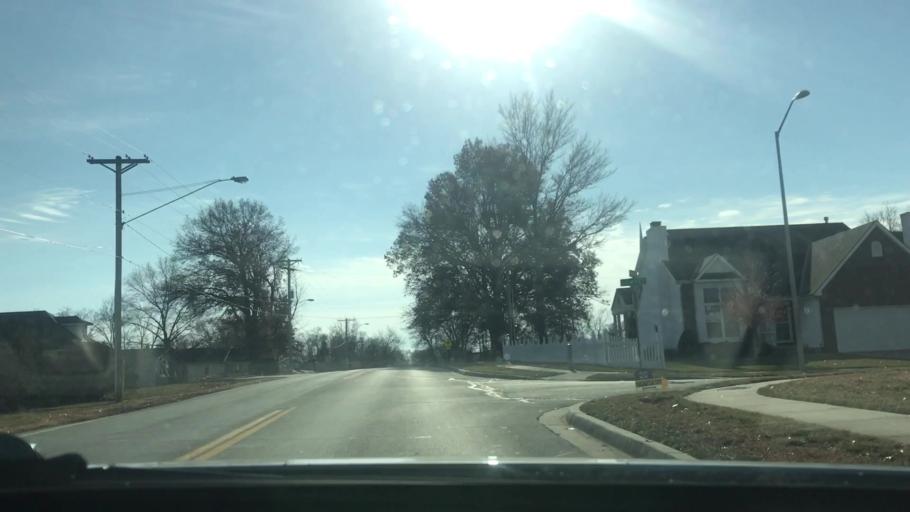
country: US
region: Missouri
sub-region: Clay County
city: Smithville
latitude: 39.3020
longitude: -94.5800
